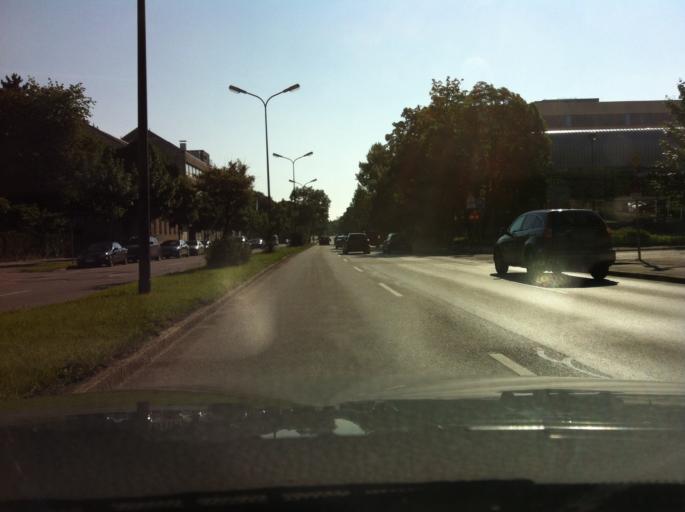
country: DE
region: Bavaria
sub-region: Upper Bavaria
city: Unterhaching
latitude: 48.1038
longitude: 11.6022
